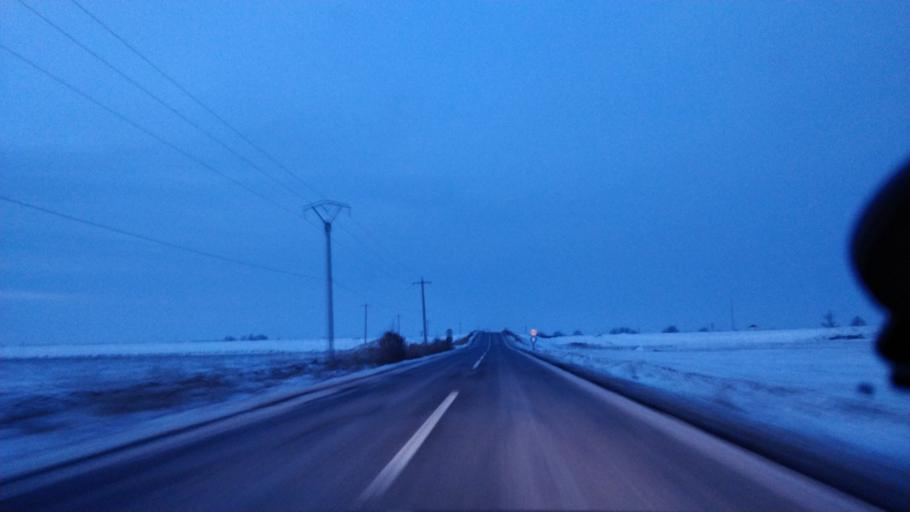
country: RO
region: Vrancea
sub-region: Comuna Nanesti
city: Nanesti
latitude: 45.5723
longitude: 27.4983
